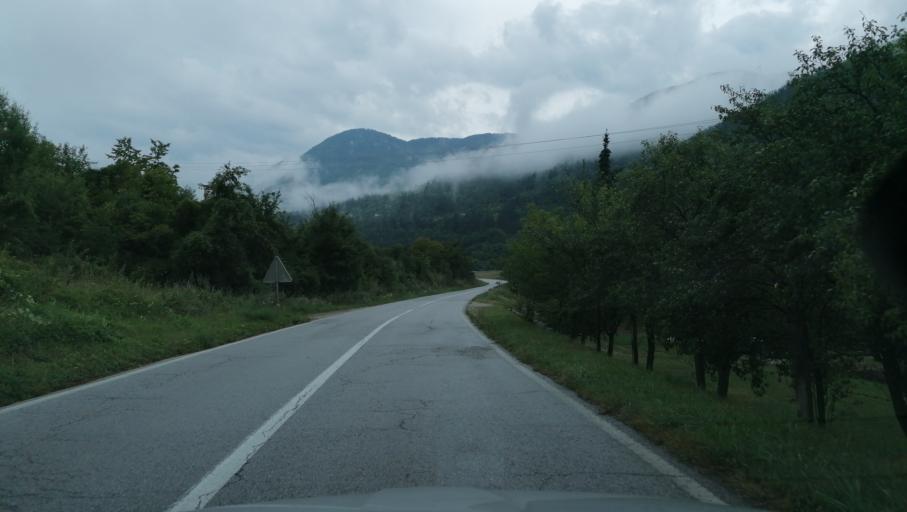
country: RS
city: Durici
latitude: 43.7616
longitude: 19.3861
